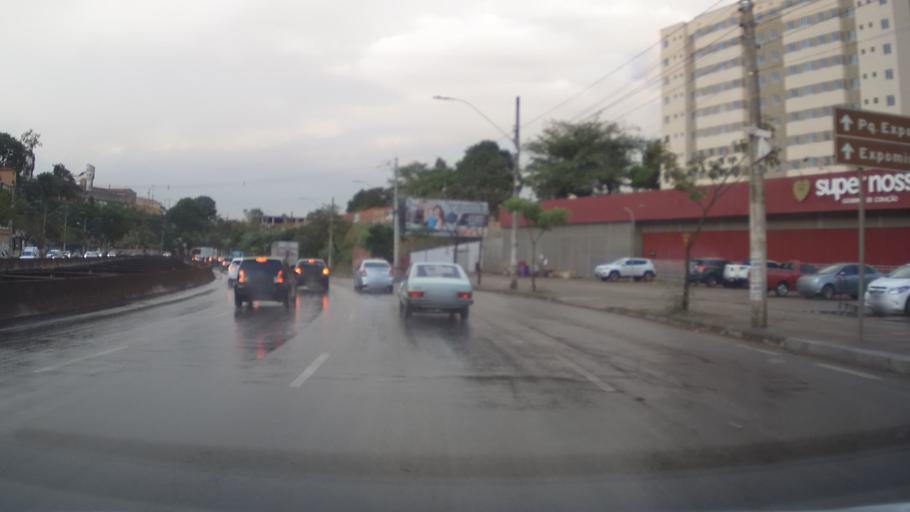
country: BR
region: Minas Gerais
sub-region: Belo Horizonte
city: Belo Horizonte
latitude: -19.9402
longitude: -43.9854
